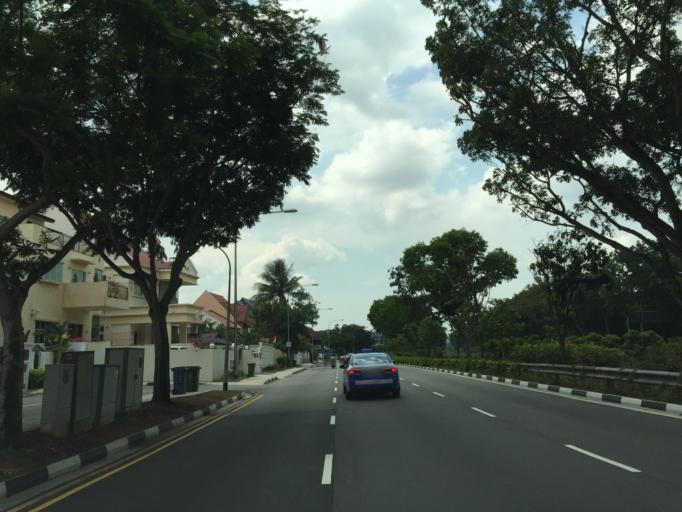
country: SG
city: Singapore
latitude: 1.3231
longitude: 103.8177
